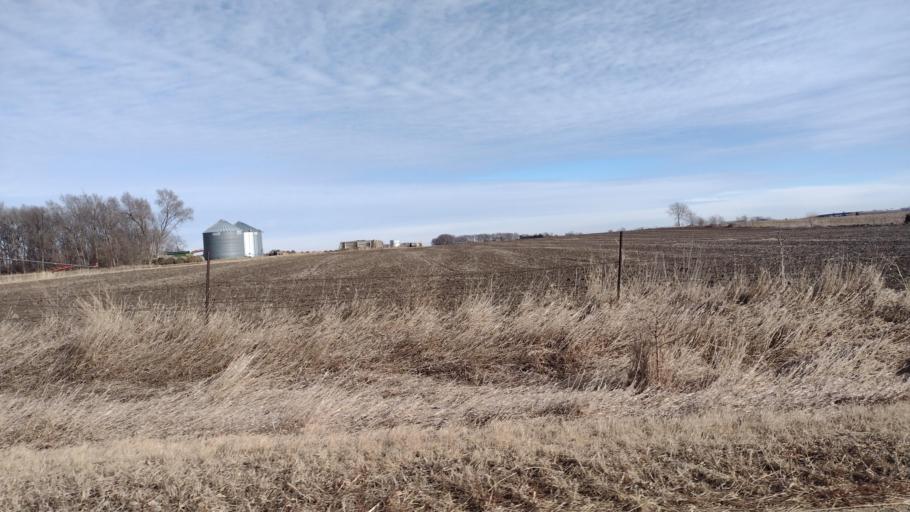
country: US
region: South Dakota
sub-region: Union County
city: Beresford
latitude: 42.9578
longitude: -96.8055
